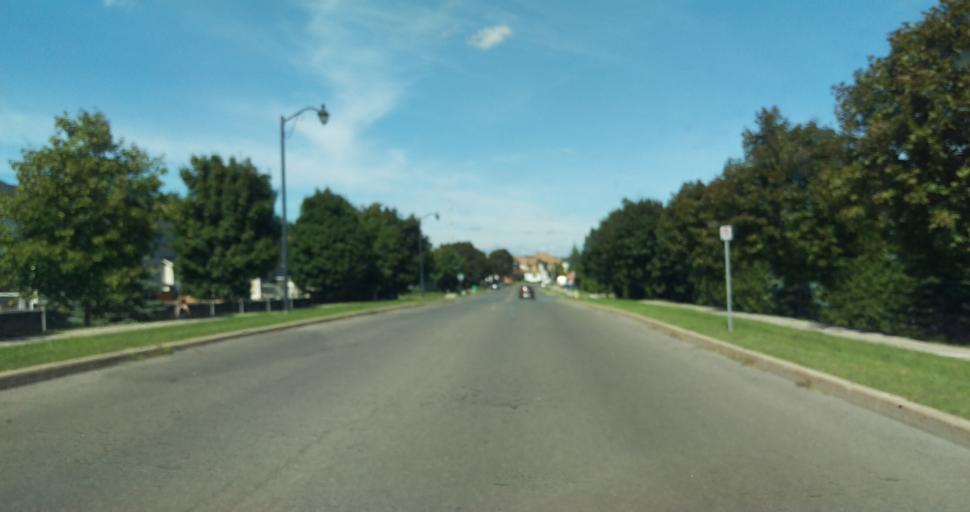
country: CA
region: Ontario
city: Clarence-Rockland
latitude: 45.4591
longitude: -75.4758
